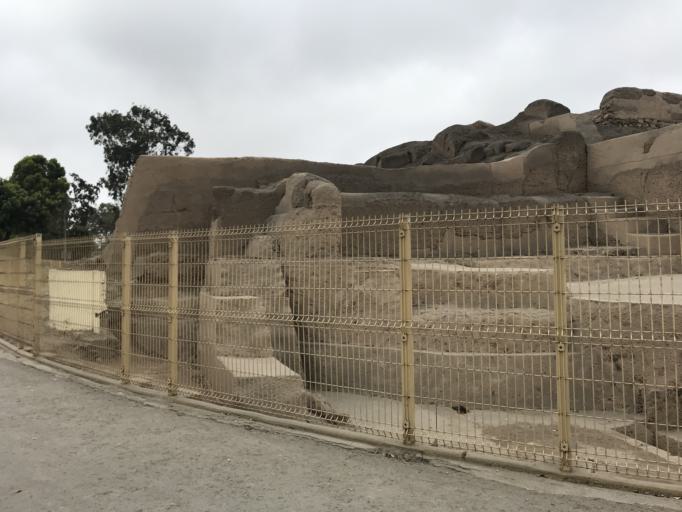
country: PE
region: Callao
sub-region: Callao
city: Callao
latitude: -12.0698
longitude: -77.0864
